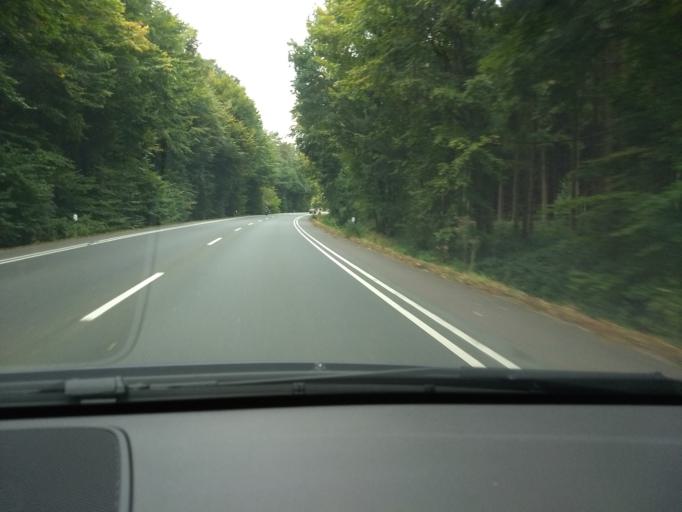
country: DE
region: North Rhine-Westphalia
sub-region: Regierungsbezirk Munster
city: Heiden
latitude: 51.8263
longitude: 6.9045
